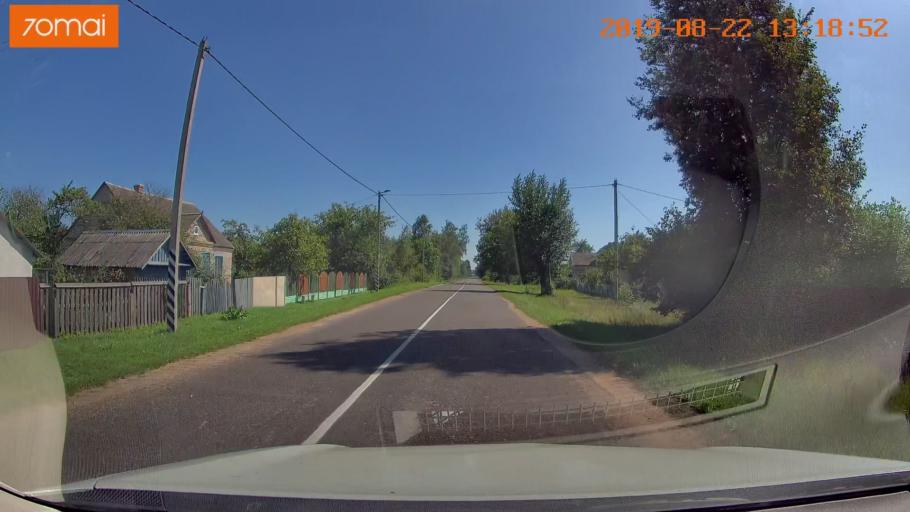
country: BY
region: Minsk
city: Urechcha
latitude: 53.2378
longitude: 27.9435
